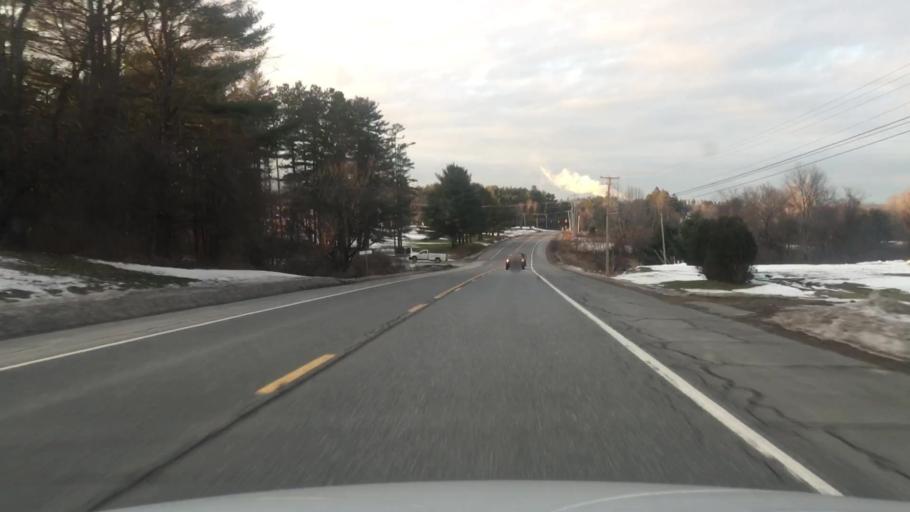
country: US
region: Maine
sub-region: Somerset County
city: Fairfield
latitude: 44.6661
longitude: -69.6281
